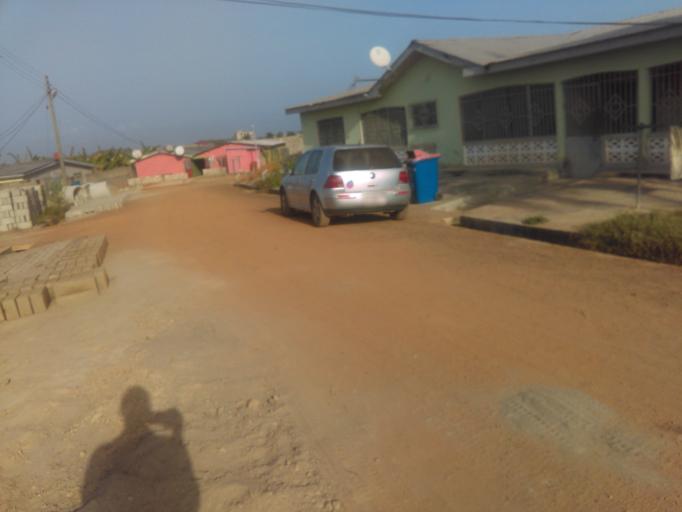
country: GH
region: Central
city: Cape Coast
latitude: 5.1084
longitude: -1.3002
